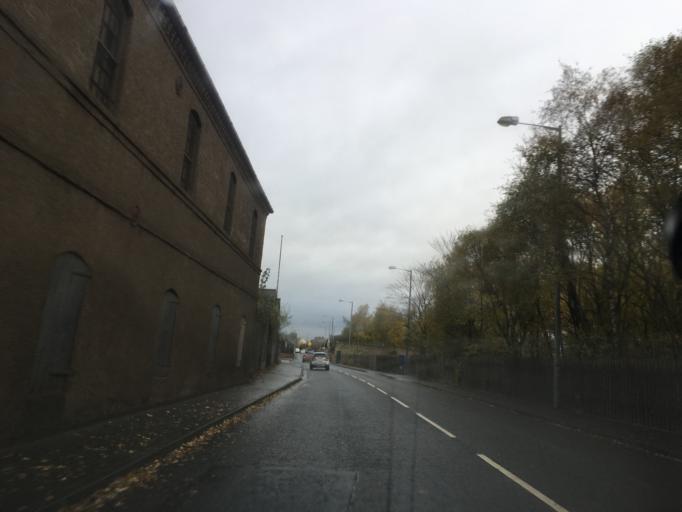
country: GB
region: Scotland
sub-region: Falkirk
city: Bo'ness
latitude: 56.0164
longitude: -3.5980
